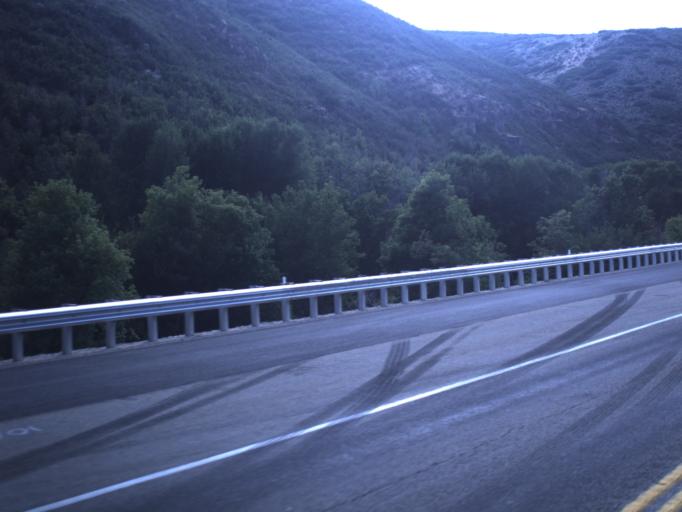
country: US
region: Utah
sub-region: Wasatch County
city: Heber
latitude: 40.4219
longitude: -111.3415
